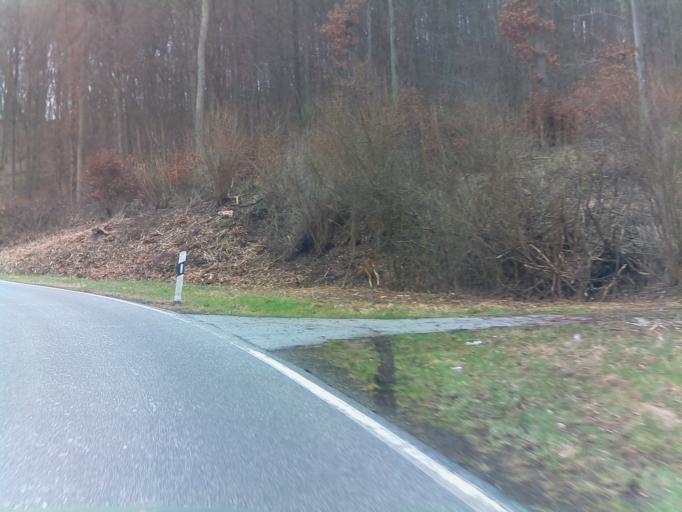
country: DE
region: Rheinland-Pfalz
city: Abtweiler
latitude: 49.7596
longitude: 7.6679
